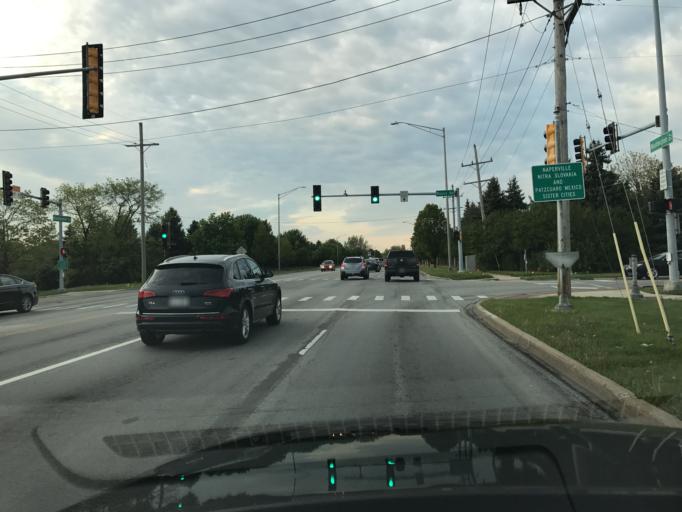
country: US
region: Illinois
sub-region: Will County
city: Bolingbrook
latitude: 41.7137
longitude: -88.1287
